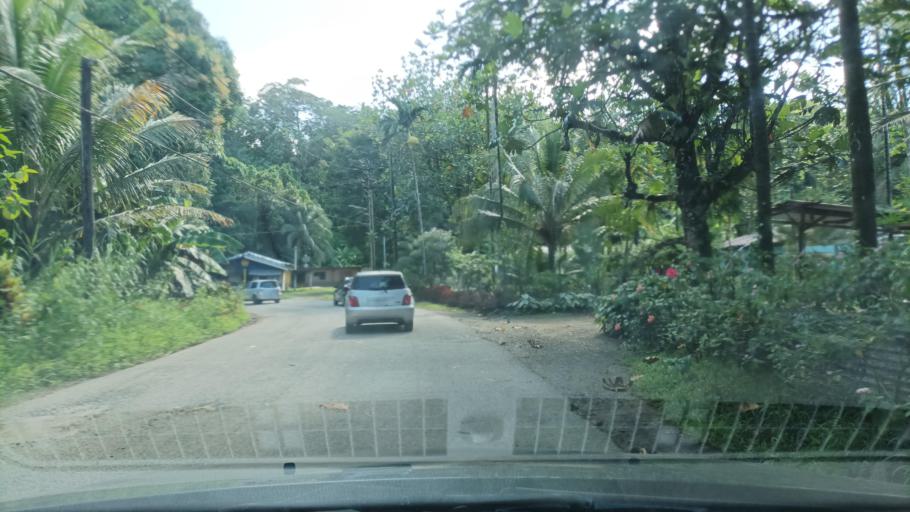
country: FM
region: Kosrae
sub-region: Lelu Municipality
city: Tofol
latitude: 5.3343
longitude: 163.0076
